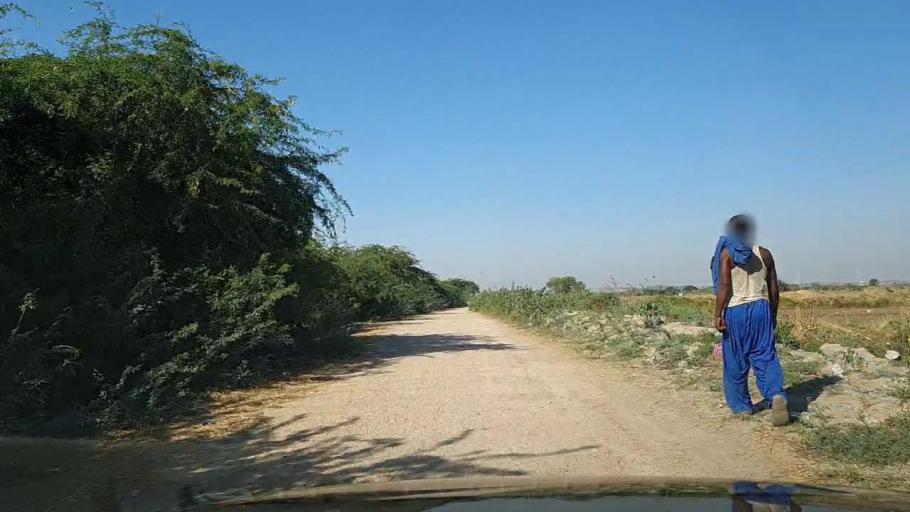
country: PK
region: Sindh
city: Thatta
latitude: 24.7189
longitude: 67.9302
